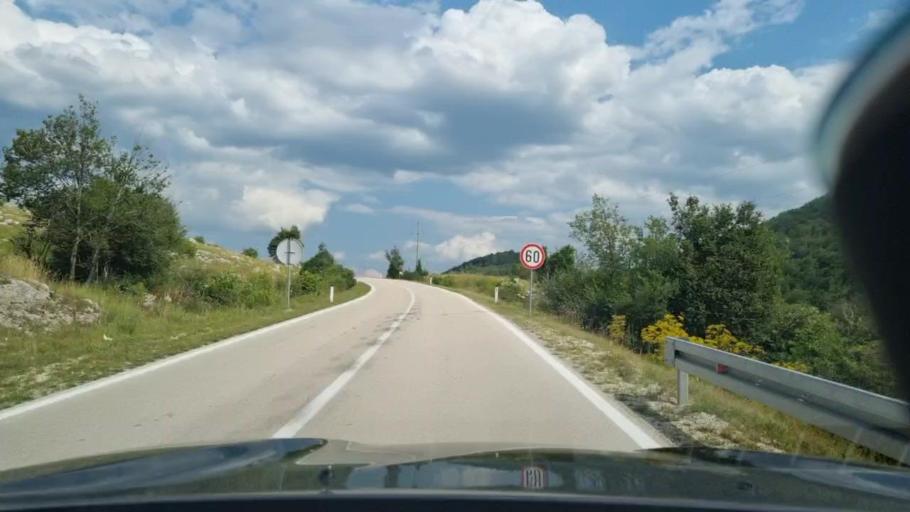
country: BA
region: Federation of Bosnia and Herzegovina
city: Bosansko Grahovo
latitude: 44.1303
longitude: 16.4925
